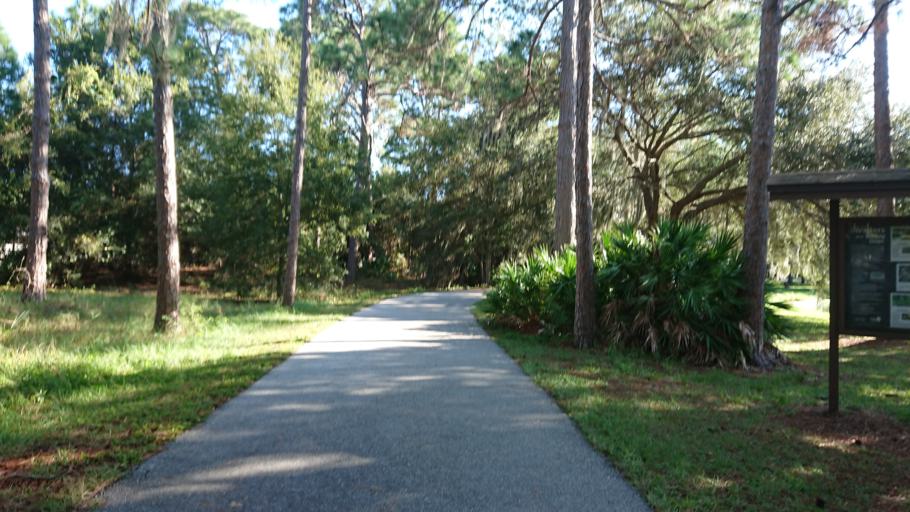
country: US
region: Florida
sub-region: Pinellas County
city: Seminole
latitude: 27.8494
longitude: -82.7752
